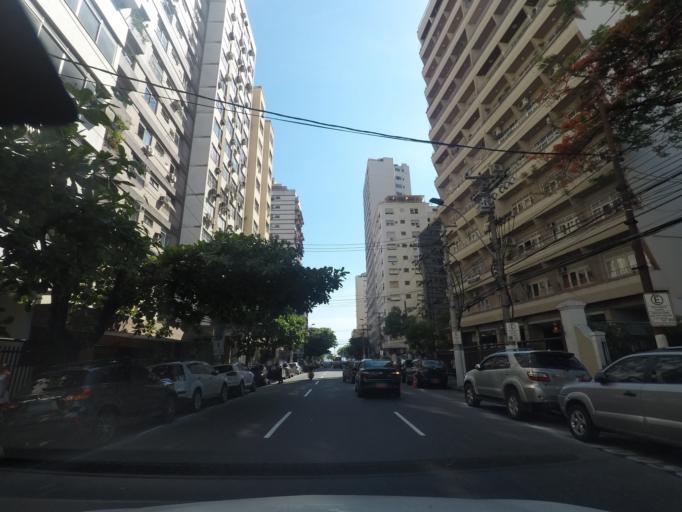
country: BR
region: Rio de Janeiro
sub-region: Niteroi
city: Niteroi
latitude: -22.9023
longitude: -43.1146
